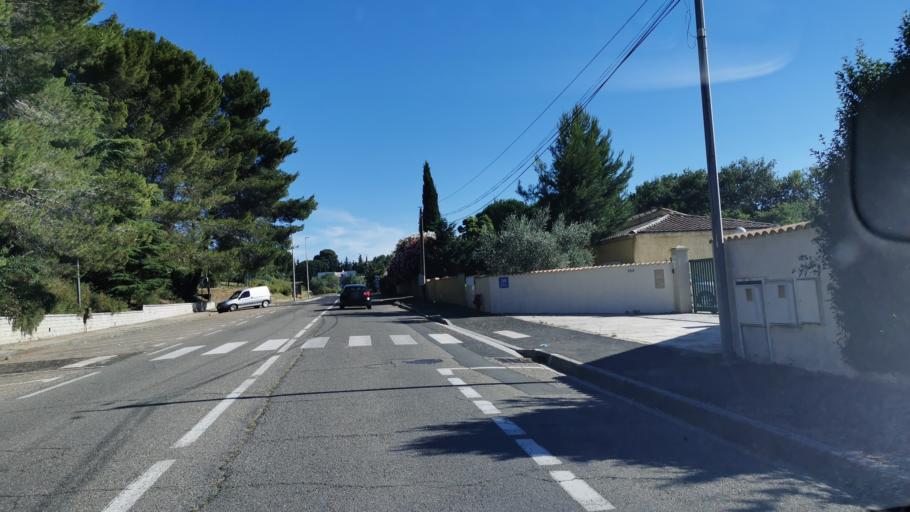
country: FR
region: Languedoc-Roussillon
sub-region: Departement de l'Herault
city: Beziers
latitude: 43.3593
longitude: 3.2125
